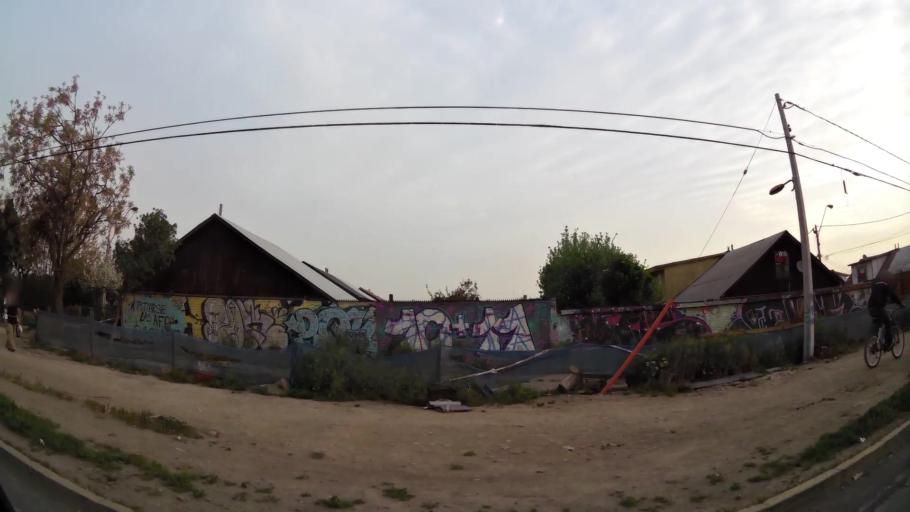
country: CL
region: Santiago Metropolitan
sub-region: Provincia de Santiago
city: Lo Prado
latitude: -33.5091
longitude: -70.7709
